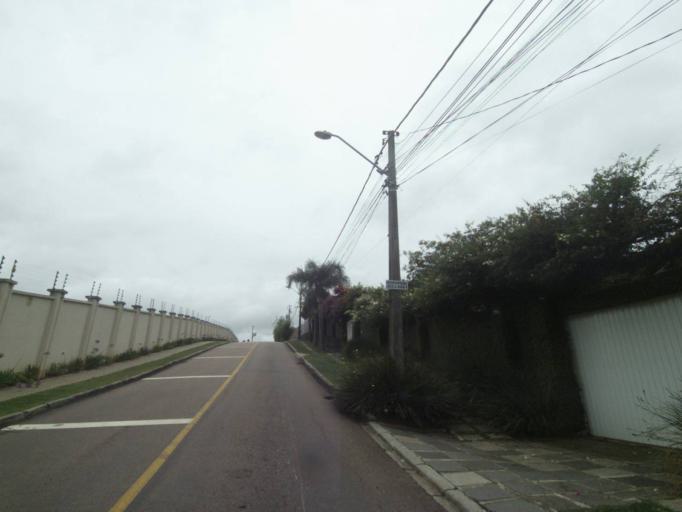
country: BR
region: Parana
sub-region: Curitiba
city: Curitiba
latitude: -25.4453
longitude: -49.3334
